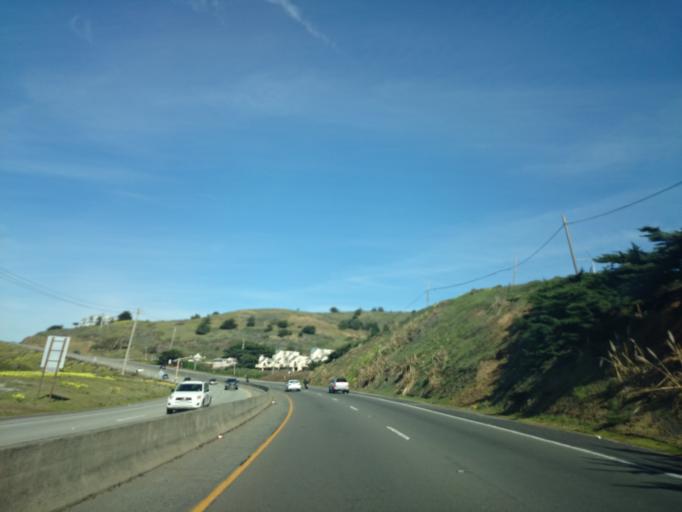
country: US
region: California
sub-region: San Mateo County
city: Pacifica
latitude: 37.6003
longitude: -122.4992
